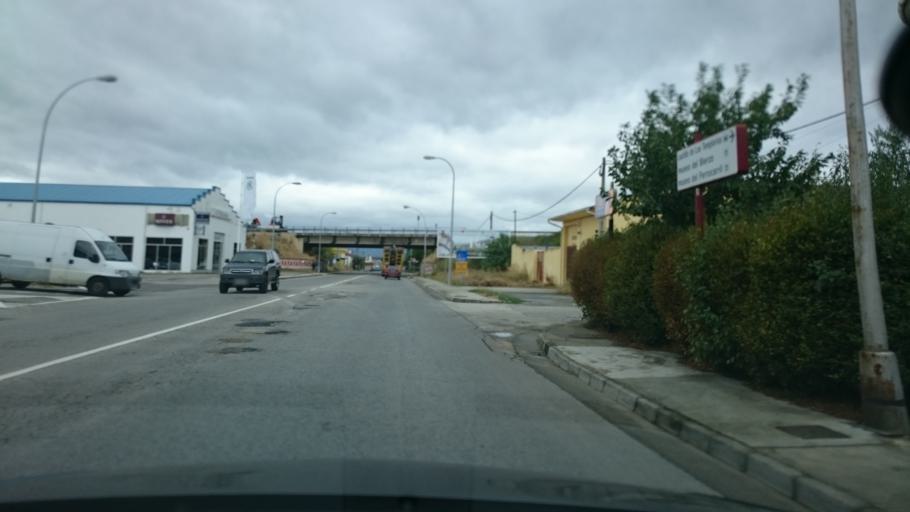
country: ES
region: Castille and Leon
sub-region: Provincia de Leon
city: Camponaraya
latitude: 42.5646
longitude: -6.6348
